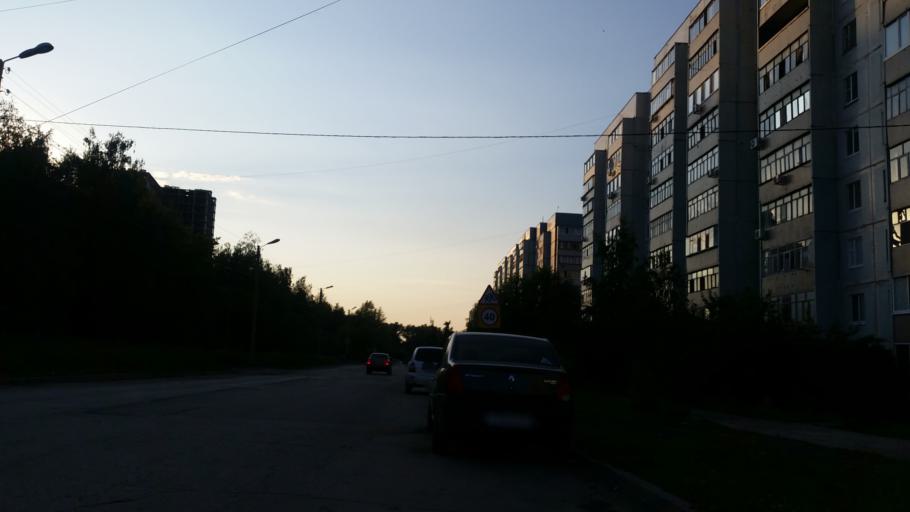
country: RU
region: Ulyanovsk
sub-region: Ulyanovskiy Rayon
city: Ulyanovsk
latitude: 54.3554
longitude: 48.3847
